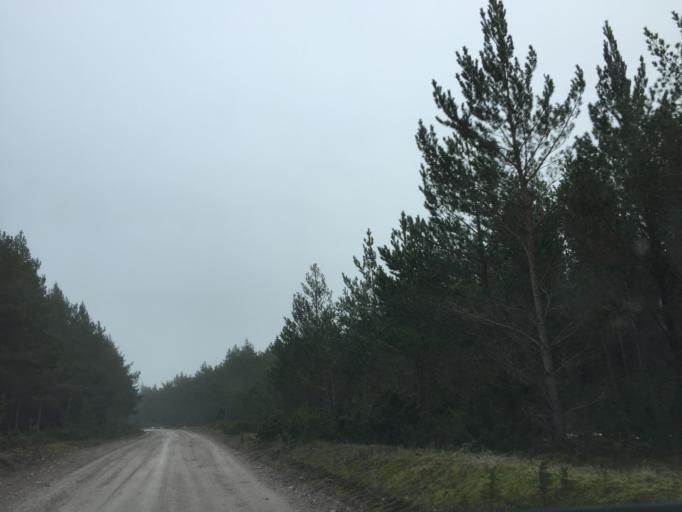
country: EE
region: Saare
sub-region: Kuressaare linn
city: Kuressaare
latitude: 58.5054
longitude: 21.9610
